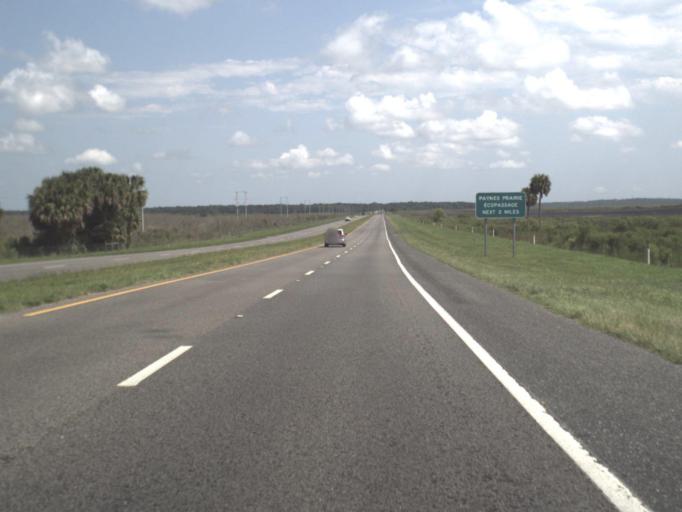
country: US
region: Florida
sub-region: Alachua County
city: Gainesville
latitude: 29.5606
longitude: -82.3317
